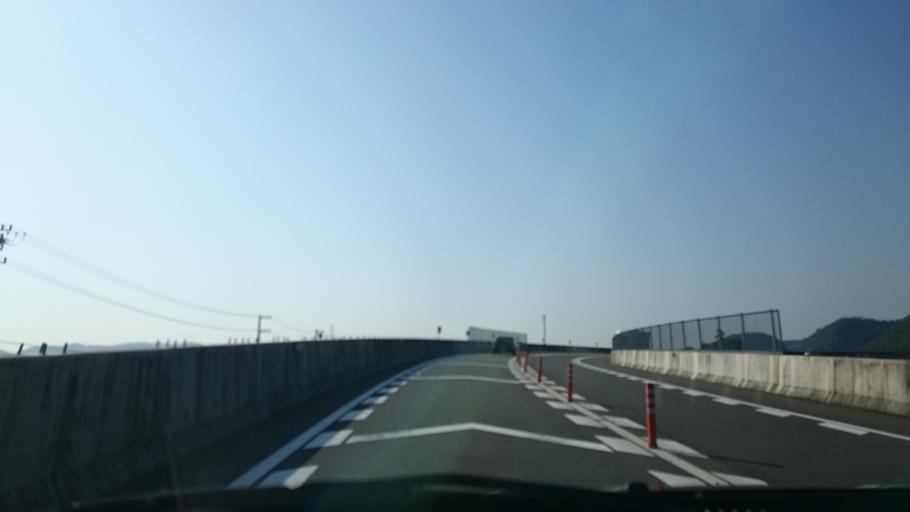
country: JP
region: Gifu
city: Minokamo
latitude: 35.4988
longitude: 137.0708
